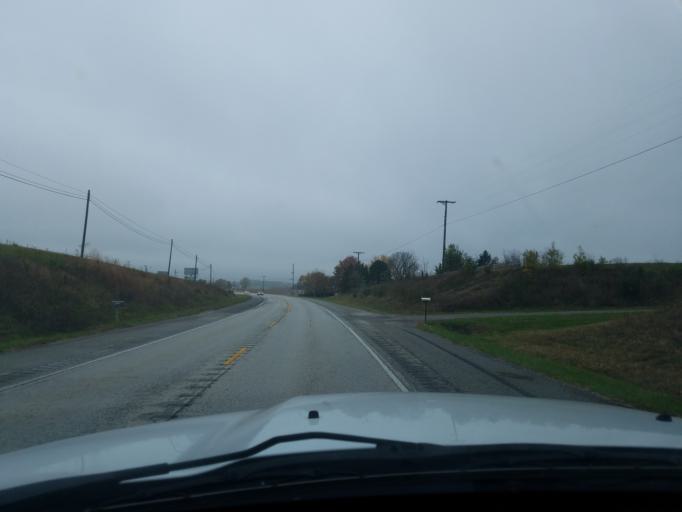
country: US
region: Kentucky
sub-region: Taylor County
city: Campbellsville
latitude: 37.3640
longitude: -85.3860
